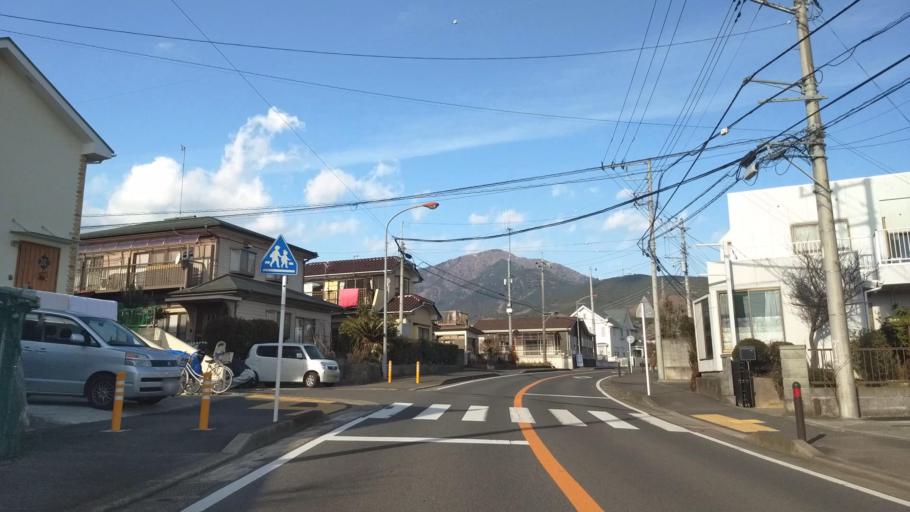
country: JP
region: Kanagawa
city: Hadano
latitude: 35.3906
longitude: 139.2348
